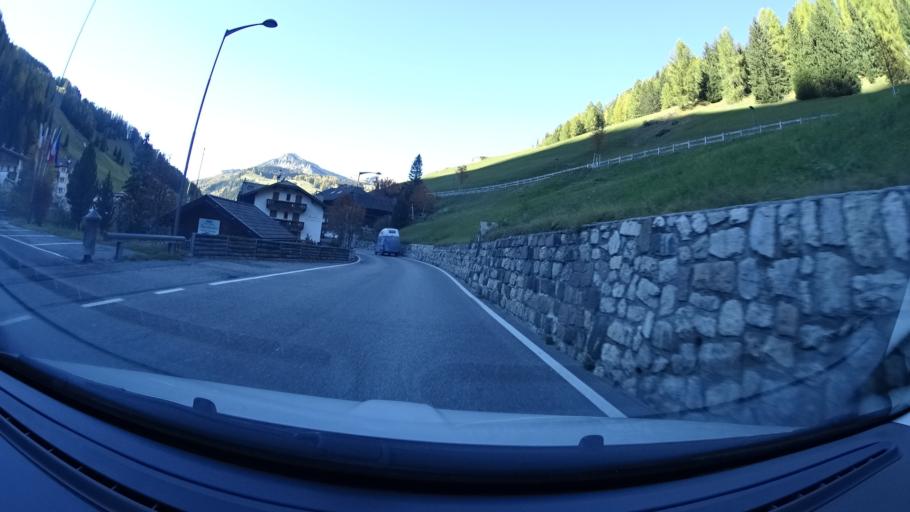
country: IT
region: Trentino-Alto Adige
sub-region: Bolzano
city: Selva
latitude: 46.5496
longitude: 11.7662
